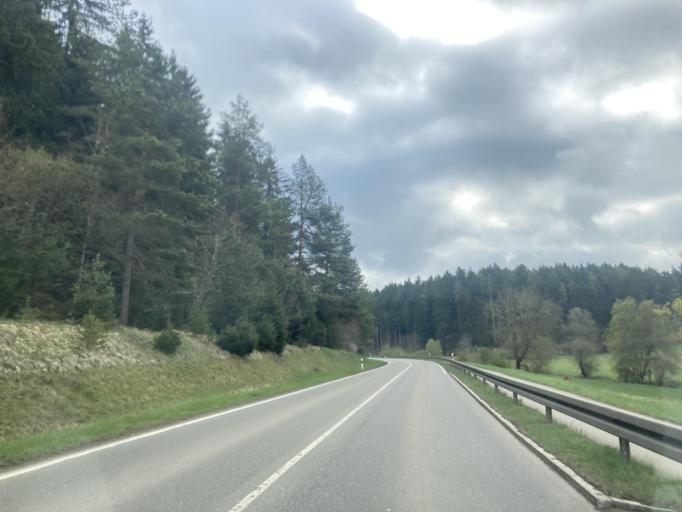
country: DE
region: Baden-Wuerttemberg
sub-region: Freiburg Region
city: Villingen-Schwenningen
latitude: 48.0315
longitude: 8.4890
